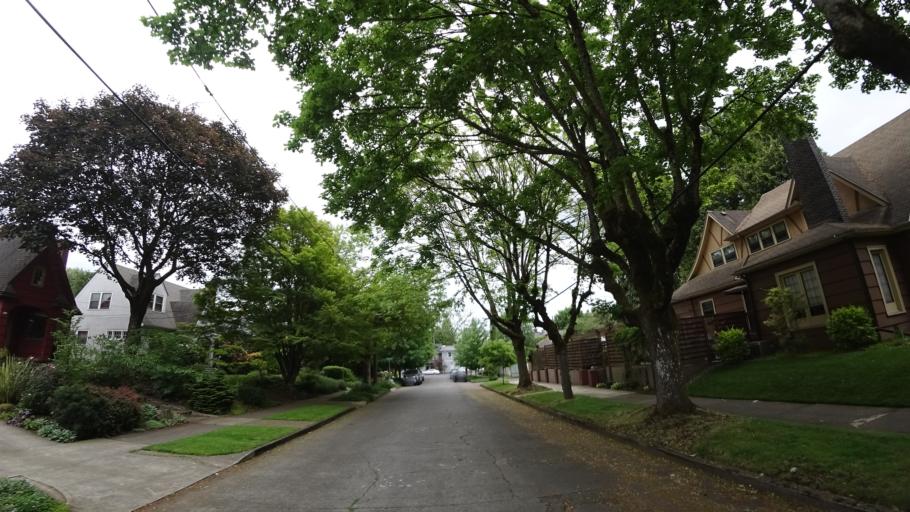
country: US
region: Oregon
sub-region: Multnomah County
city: Portland
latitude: 45.5201
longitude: -122.6174
